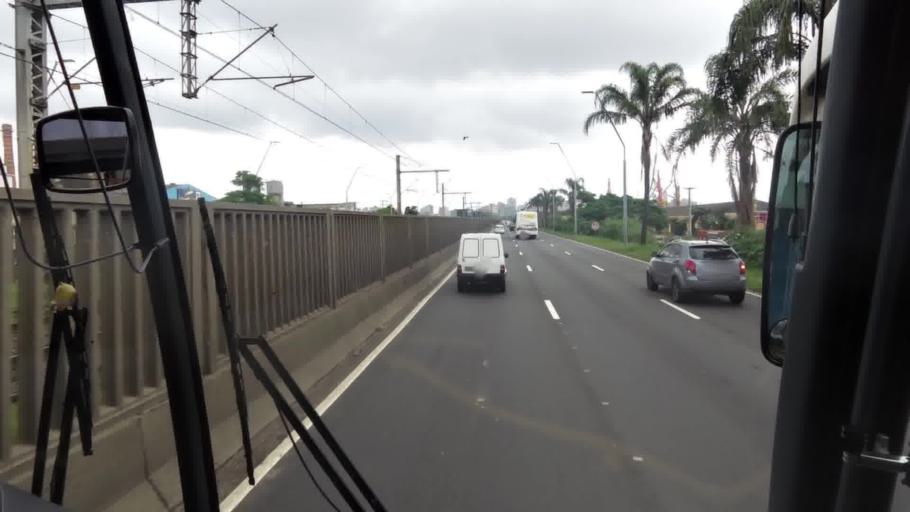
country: BR
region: Rio Grande do Sul
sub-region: Porto Alegre
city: Porto Alegre
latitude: -30.0095
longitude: -51.2111
